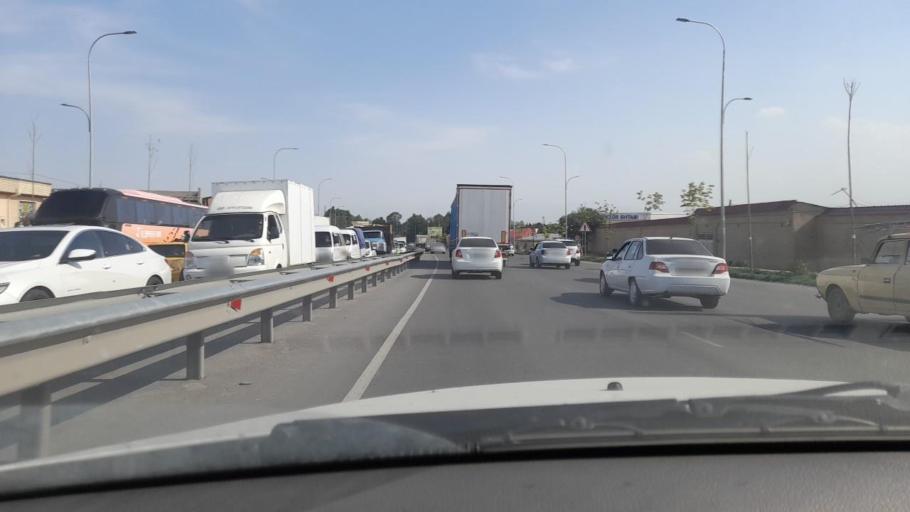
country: UZ
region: Samarqand
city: Samarqand
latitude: 39.6794
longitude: 67.0051
